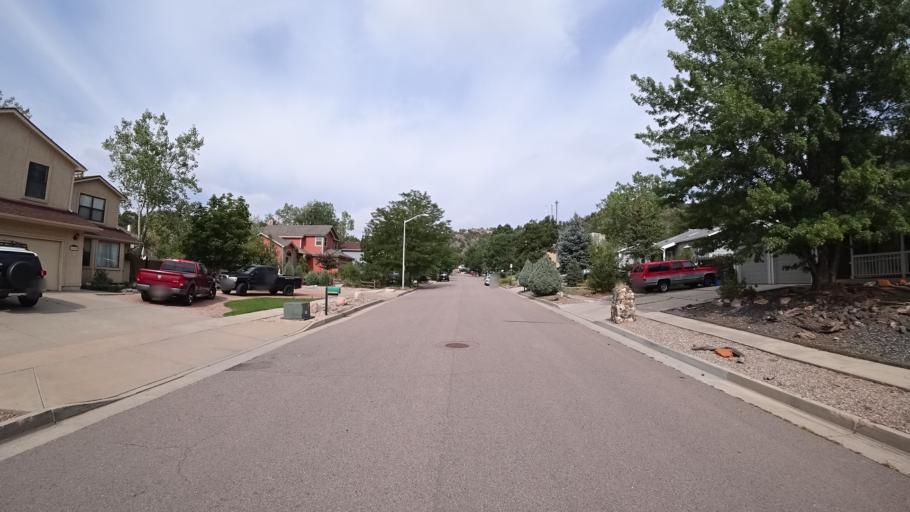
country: US
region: Colorado
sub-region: El Paso County
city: Colorado Springs
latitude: 38.8926
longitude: -104.7922
